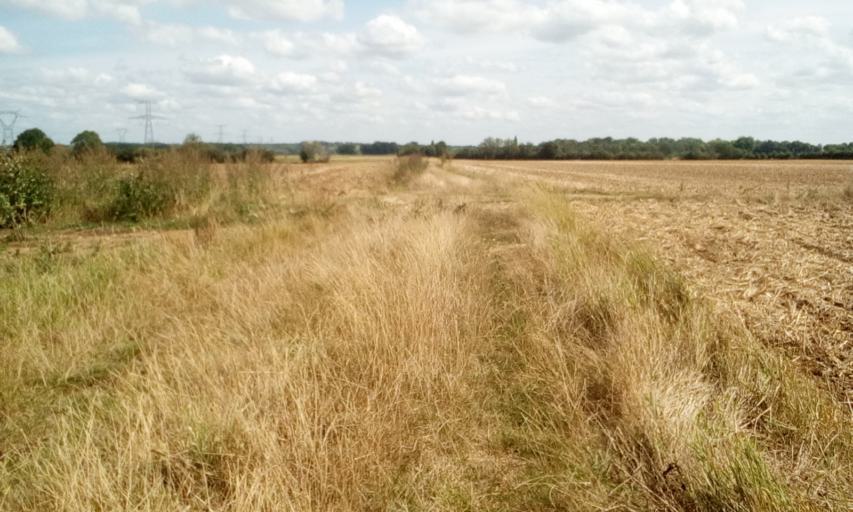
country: FR
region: Lower Normandy
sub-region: Departement du Calvados
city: Bellengreville
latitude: 49.1318
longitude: -0.2116
